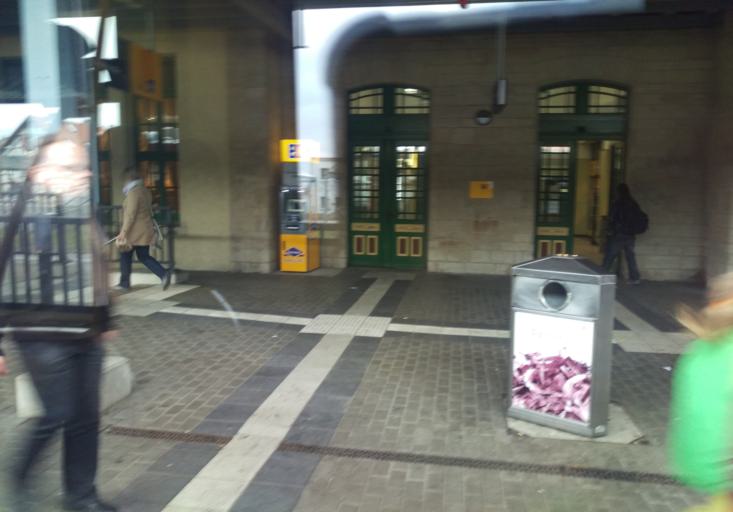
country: DE
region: Saxony-Anhalt
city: Wernigerode
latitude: 51.8401
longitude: 10.7890
